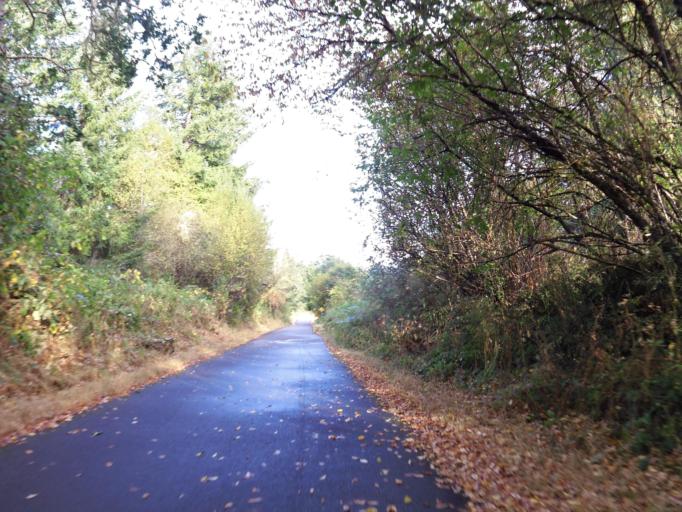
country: US
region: Washington
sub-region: Thurston County
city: Rainier
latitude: 46.9071
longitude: -122.7747
